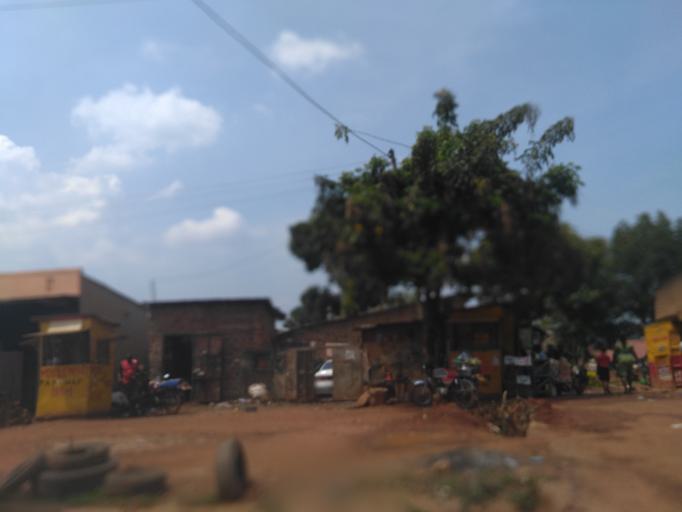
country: UG
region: Central Region
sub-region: Wakiso District
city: Kireka
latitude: 0.4549
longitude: 32.6063
